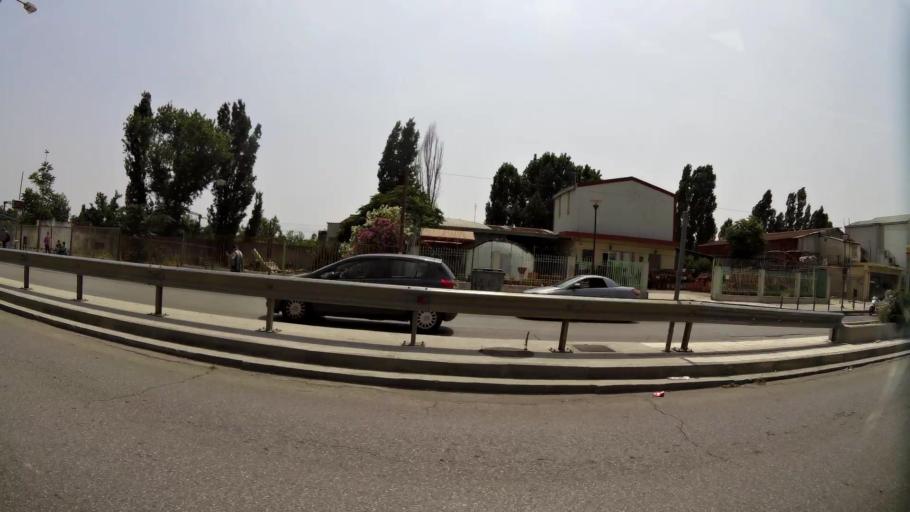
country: GR
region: Central Macedonia
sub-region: Nomos Thessalonikis
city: Menemeni
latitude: 40.6644
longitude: 22.8955
